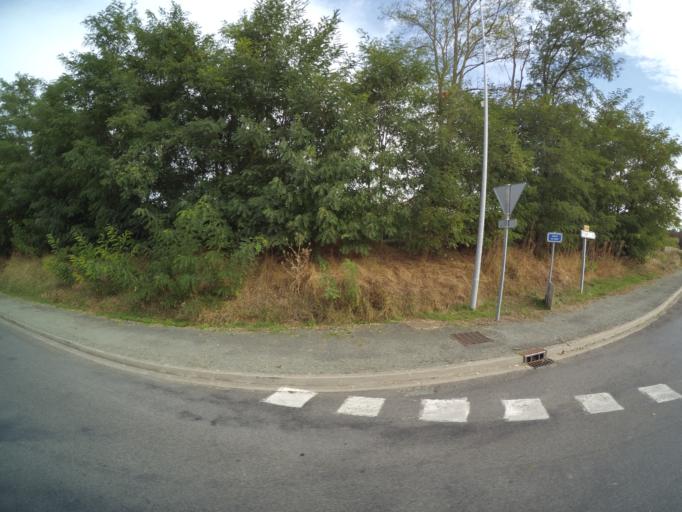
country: FR
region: Pays de la Loire
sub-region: Departement de Maine-et-Loire
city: Vihiers
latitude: 47.2107
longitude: -0.5918
